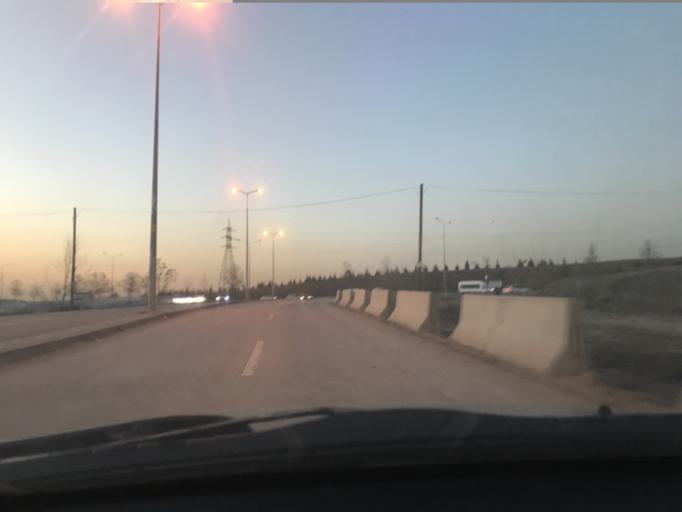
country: TR
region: Ankara
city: Batikent
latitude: 39.9155
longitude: 32.7728
